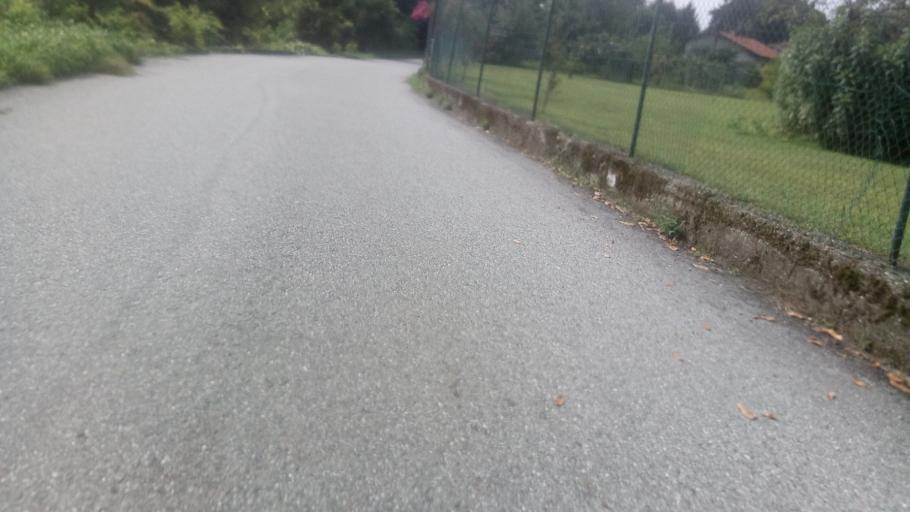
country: IT
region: Piedmont
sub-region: Provincia di Torino
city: Parella
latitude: 45.4333
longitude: 7.7933
